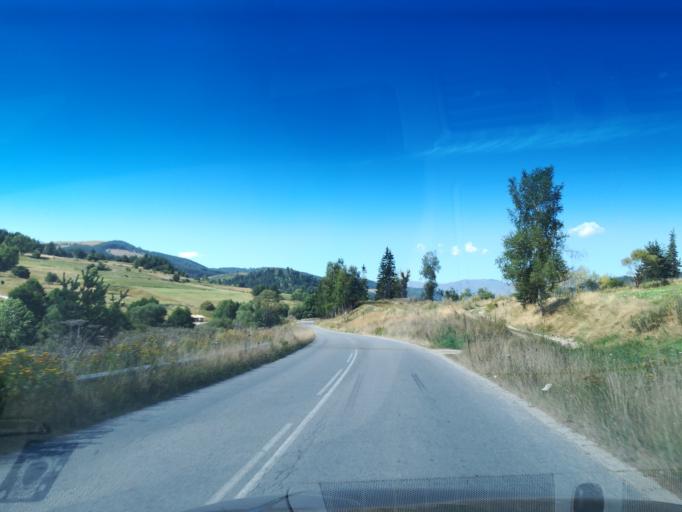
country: BG
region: Sofiya
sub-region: Obshtina Koprivshtitsa
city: Koprivshtitsa
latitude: 42.6124
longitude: 24.3746
